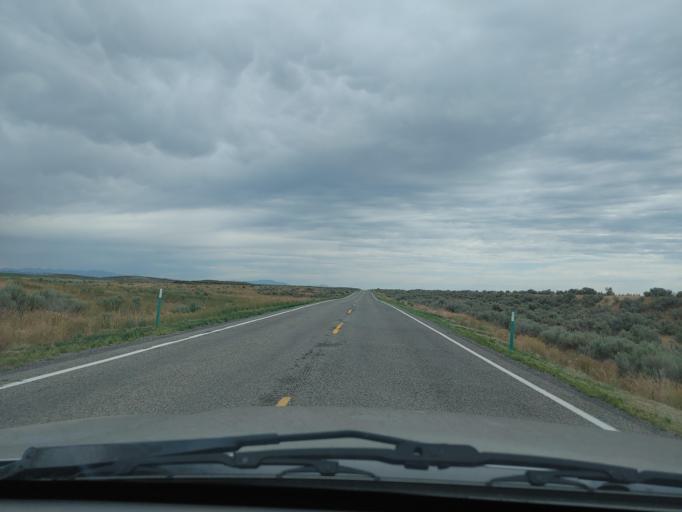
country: US
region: Idaho
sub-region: Lincoln County
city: Shoshone
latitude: 43.0671
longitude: -114.1175
